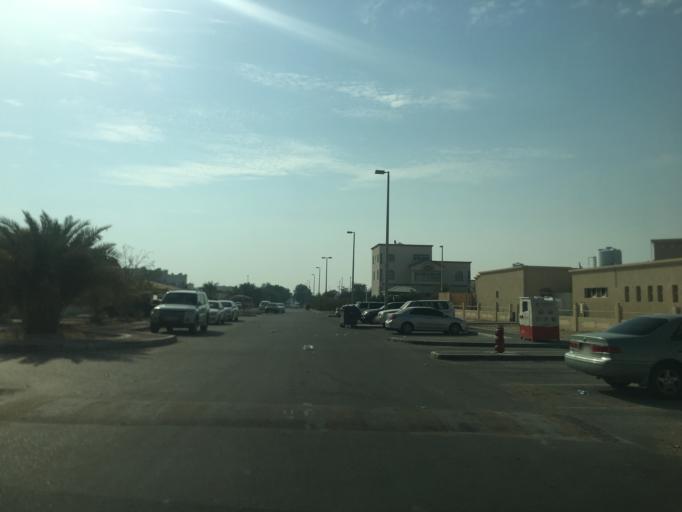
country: AE
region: Abu Dhabi
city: Abu Dhabi
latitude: 24.2997
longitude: 54.6510
